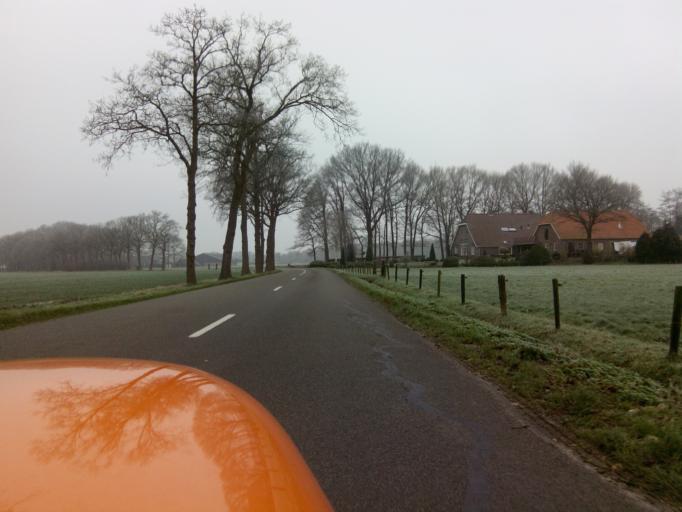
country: NL
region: Gelderland
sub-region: Gemeente Barneveld
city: Voorthuizen
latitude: 52.1925
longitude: 5.6018
